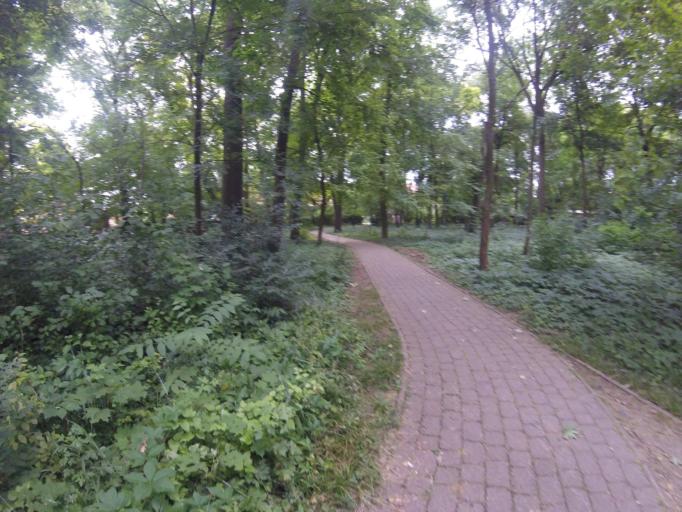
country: HU
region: Baranya
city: Boly
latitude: 45.9687
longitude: 18.5140
